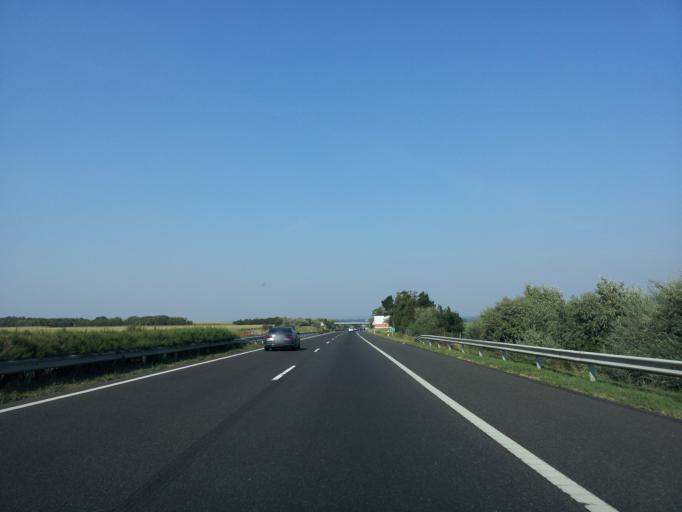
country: HU
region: Fejer
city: Szabadbattyan
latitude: 47.0844
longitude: 18.3580
